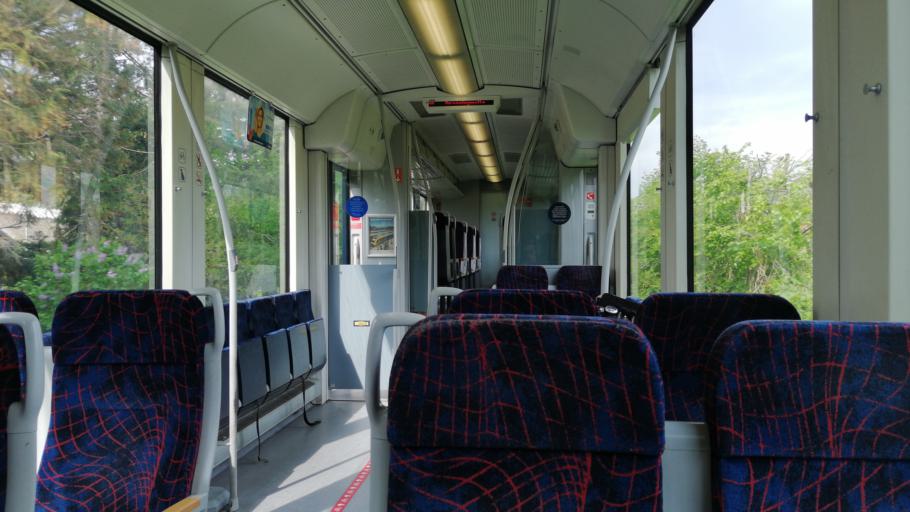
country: DK
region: Capital Region
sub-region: Helsingor Kommune
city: Hornbaek
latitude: 56.0971
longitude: 12.3921
